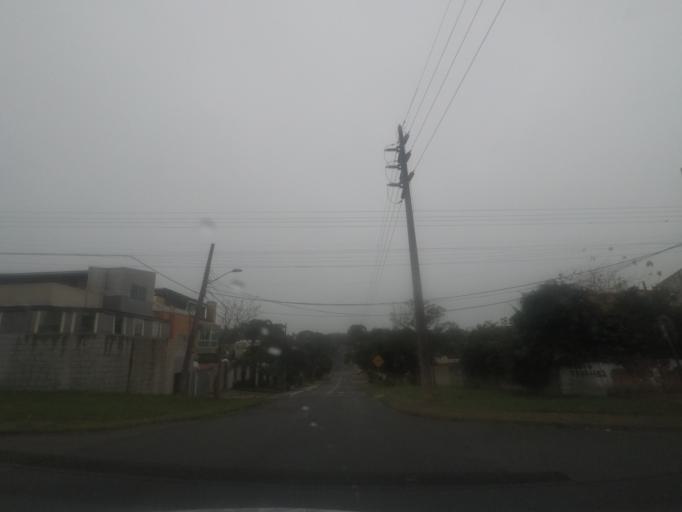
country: BR
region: Parana
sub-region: Curitiba
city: Curitiba
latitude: -25.4097
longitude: -49.2817
